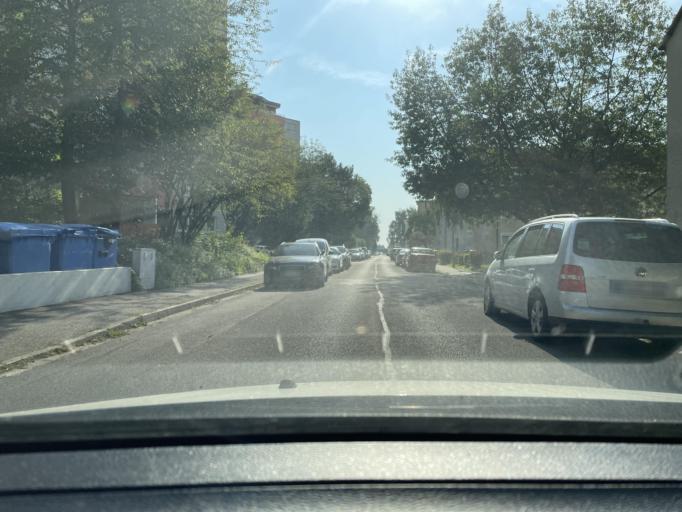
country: DE
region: Bavaria
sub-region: Upper Bavaria
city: Muehldorf
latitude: 48.2464
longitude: 12.5148
